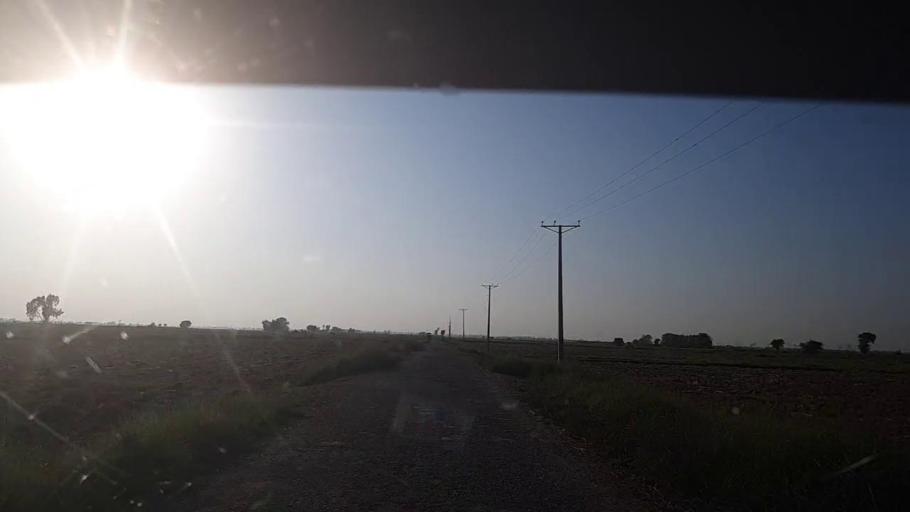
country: PK
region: Sindh
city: Ratodero
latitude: 27.8521
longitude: 68.2226
